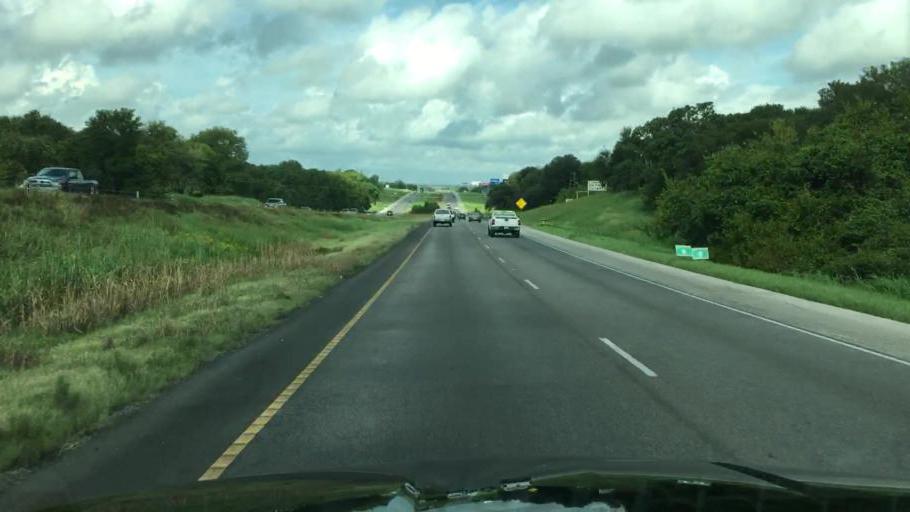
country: US
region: Texas
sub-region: Bastrop County
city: Wyldwood
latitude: 30.1546
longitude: -97.4934
